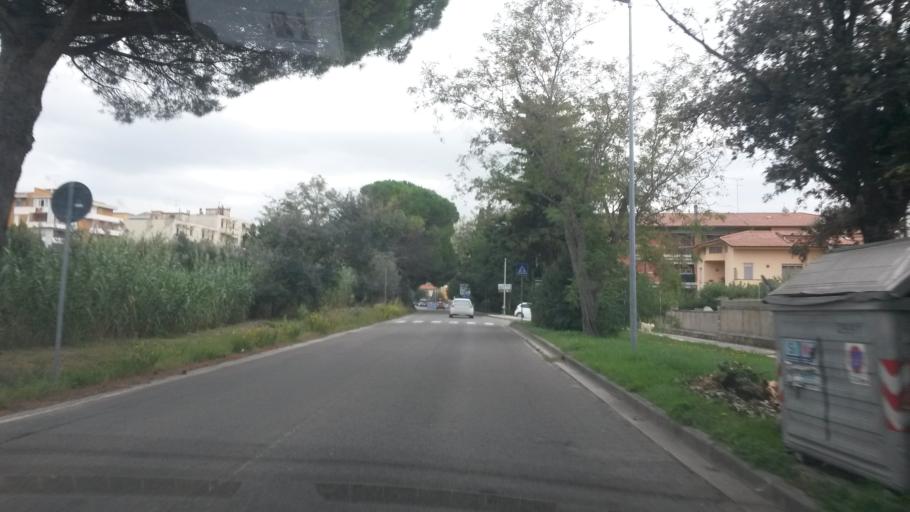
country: IT
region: Tuscany
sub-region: Provincia di Livorno
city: Rosignano Solvay-Castiglioncello
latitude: 43.3995
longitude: 10.4397
